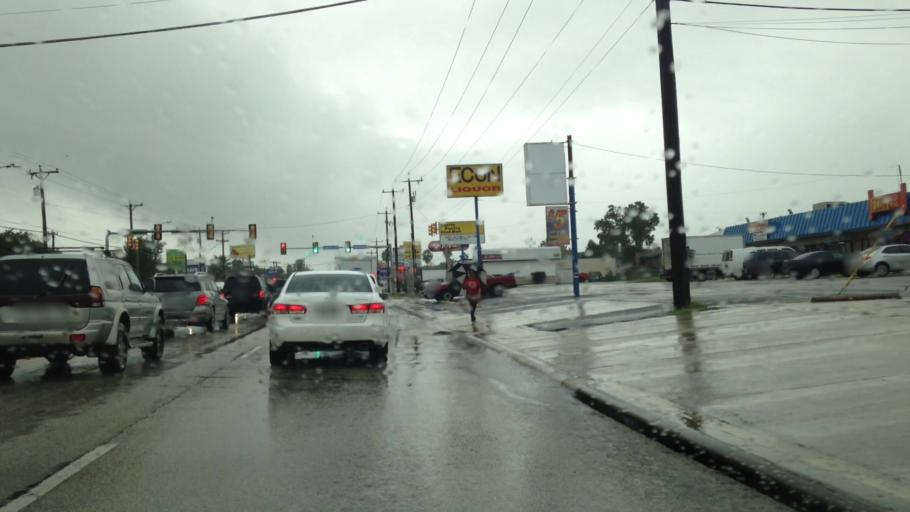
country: US
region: Texas
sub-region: Bexar County
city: Windcrest
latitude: 29.5227
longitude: -98.4110
